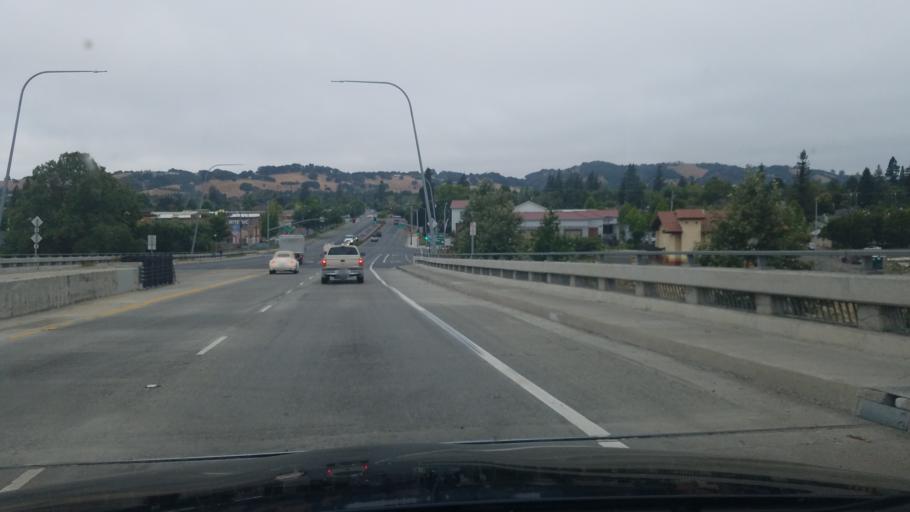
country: US
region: California
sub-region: Napa County
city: Napa
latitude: 38.2817
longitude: -122.2871
